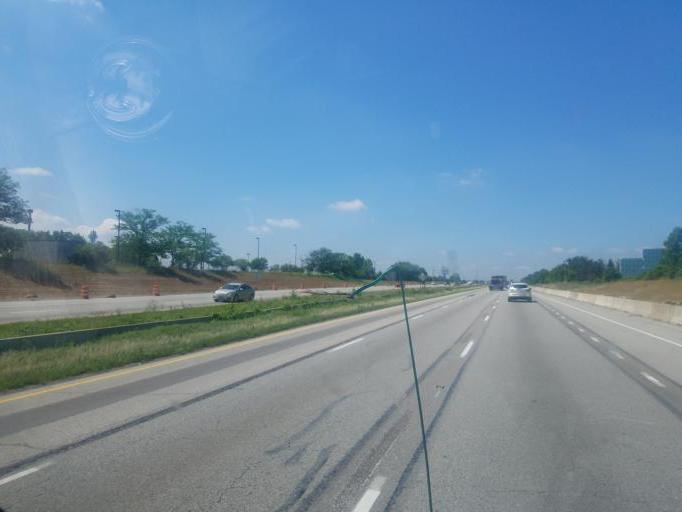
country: US
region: Ohio
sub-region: Warren County
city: Kings Mills
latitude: 39.3532
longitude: -84.2680
